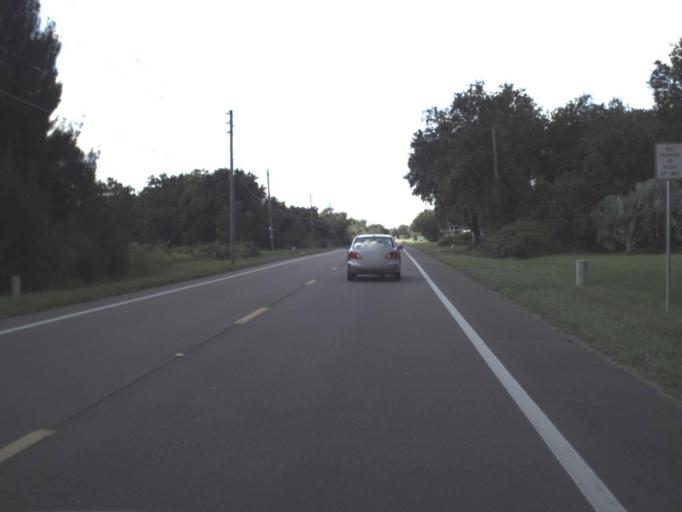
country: US
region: Florida
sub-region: DeSoto County
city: Nocatee
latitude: 27.1777
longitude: -81.8734
